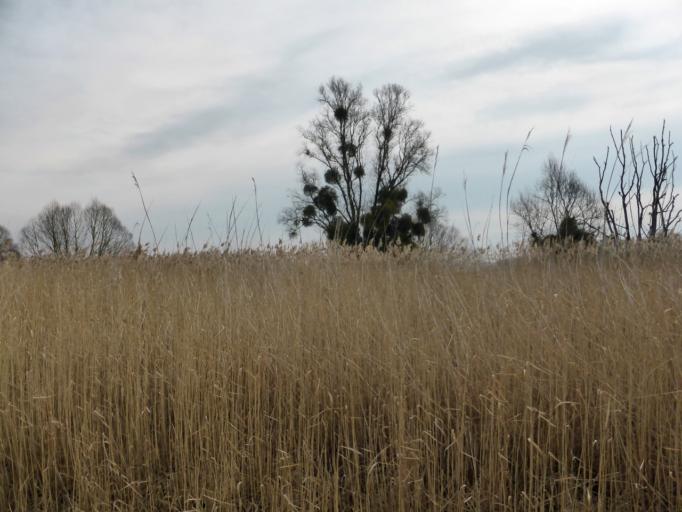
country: FR
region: Champagne-Ardenne
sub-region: Departement de l'Aube
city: Lusigny-sur-Barse
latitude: 48.2779
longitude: 4.3060
